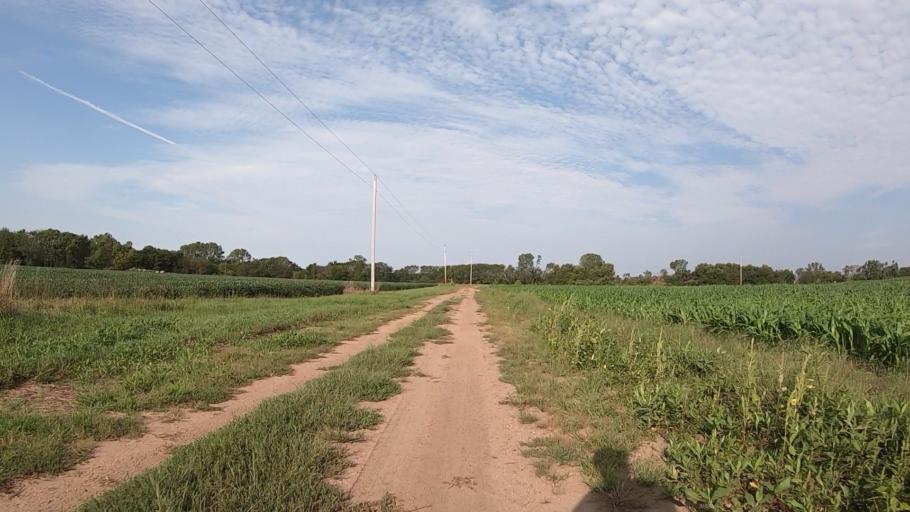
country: US
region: Kansas
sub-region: Washington County
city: Washington
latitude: 39.6714
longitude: -96.9454
